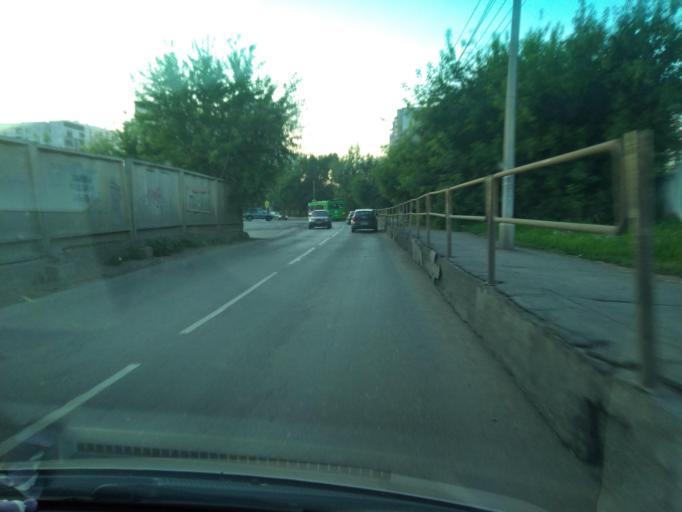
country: RU
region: Krasnoyarskiy
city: Krasnoyarsk
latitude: 55.9849
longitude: 92.8713
